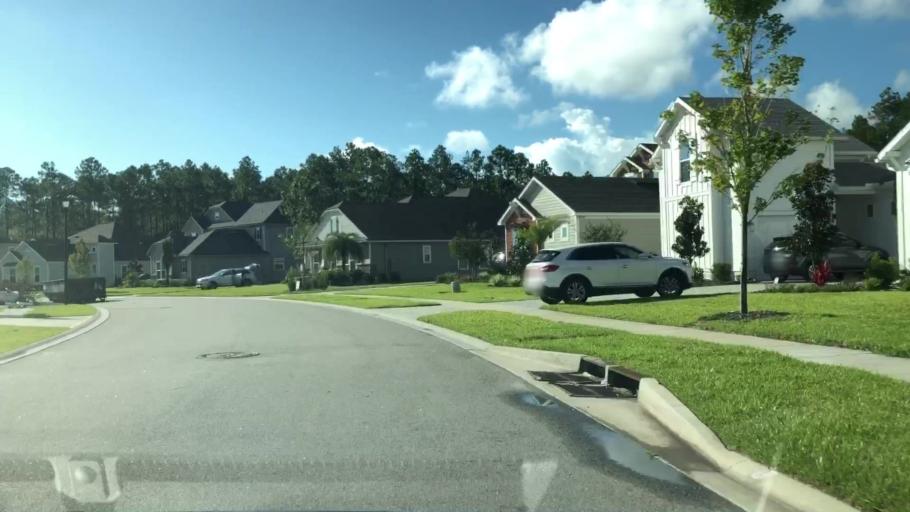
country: US
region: Florida
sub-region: Saint Johns County
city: Palm Valley
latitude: 30.1340
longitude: -81.4139
